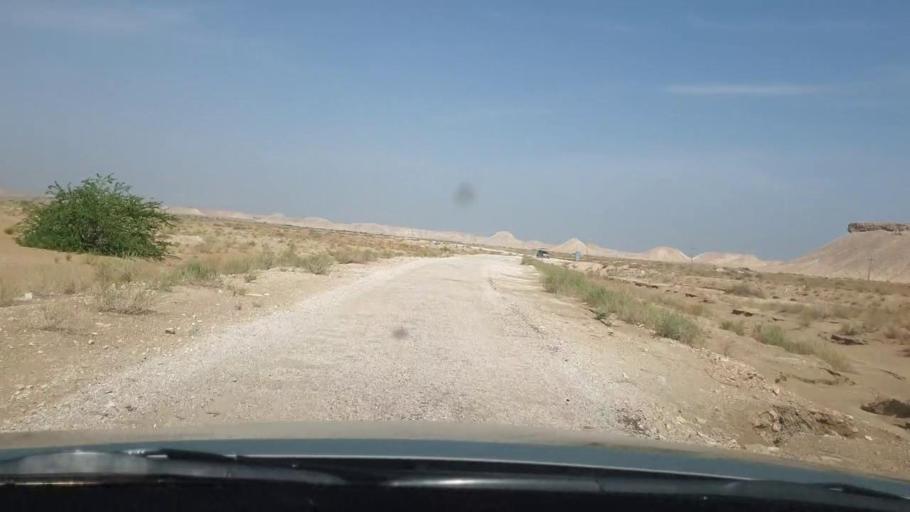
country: PK
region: Sindh
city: Kot Diji
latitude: 27.3267
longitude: 68.8104
